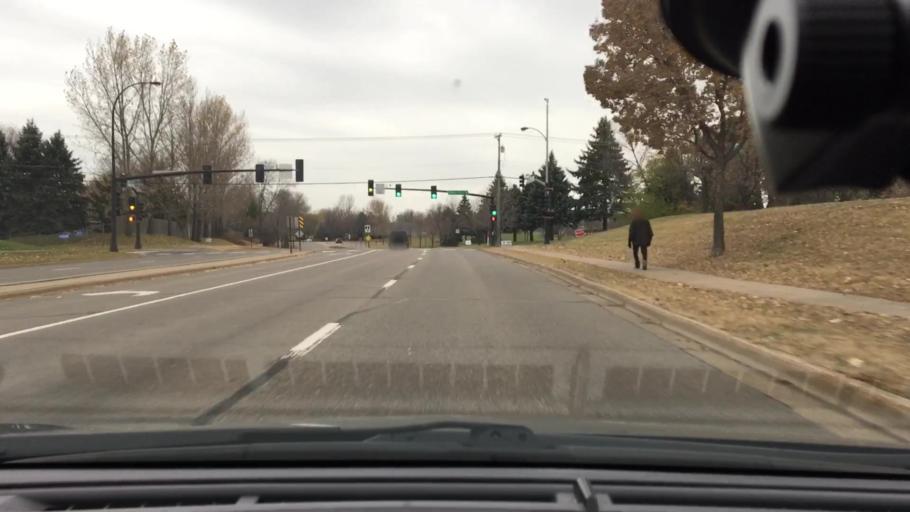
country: US
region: Minnesota
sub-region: Hennepin County
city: Maple Grove
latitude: 45.1169
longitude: -93.4519
